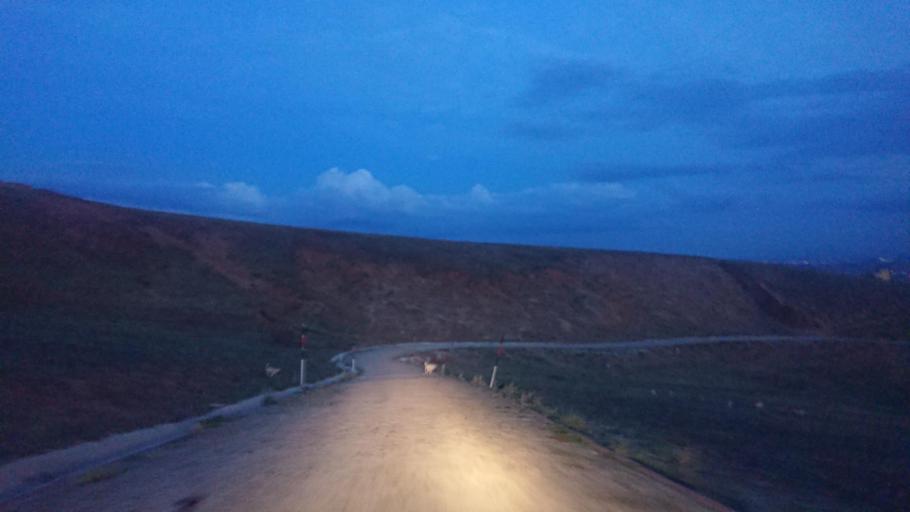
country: TR
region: Aksaray
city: Ortakoy
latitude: 38.6363
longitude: 34.0179
